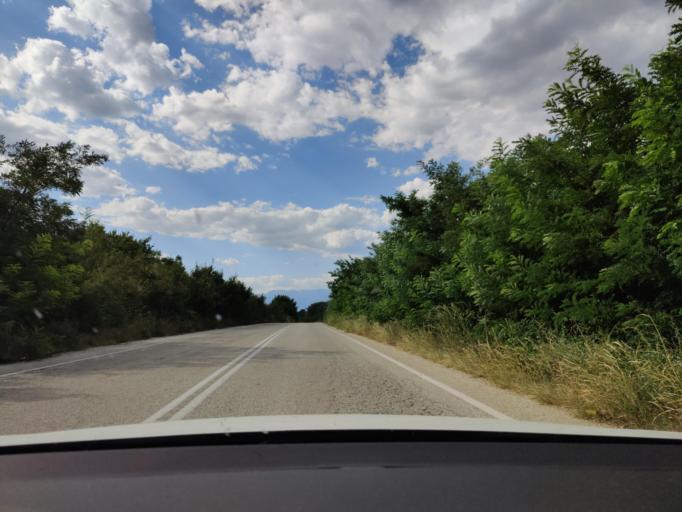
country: GR
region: Central Macedonia
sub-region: Nomos Serron
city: Strymoniko
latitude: 41.0585
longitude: 23.3123
